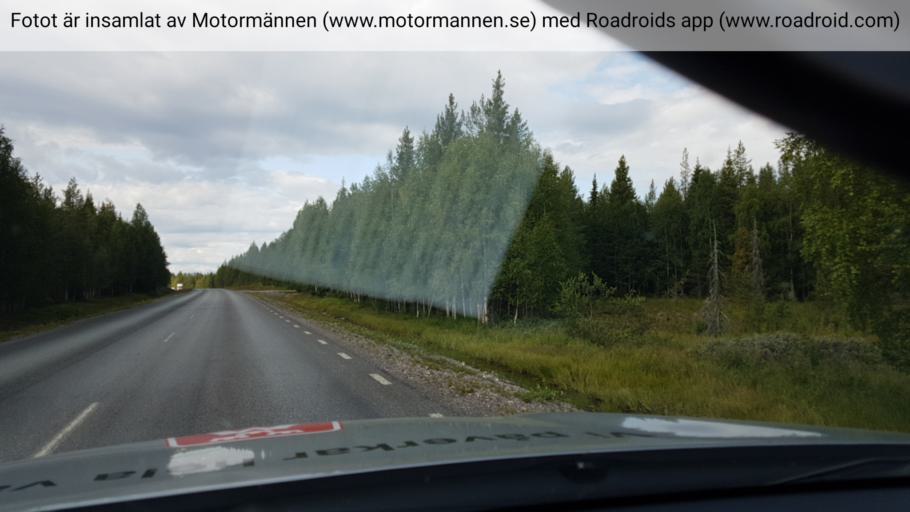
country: SE
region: Norrbotten
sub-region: Arvidsjaurs Kommun
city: Arvidsjaur
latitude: 65.5892
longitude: 19.4700
